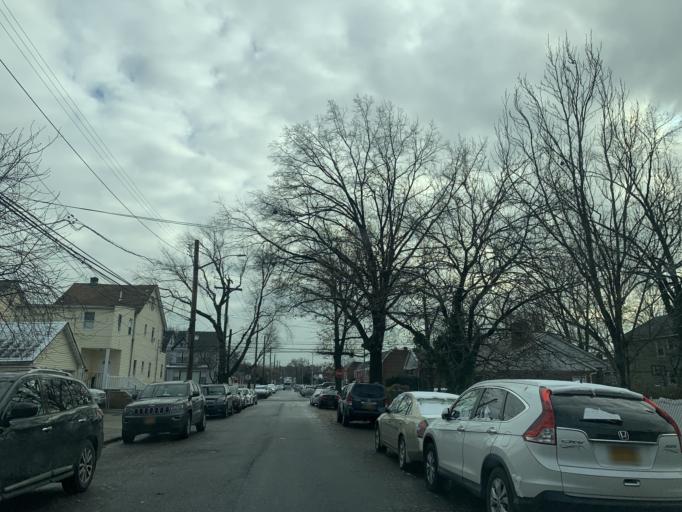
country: US
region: New York
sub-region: Queens County
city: Jamaica
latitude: 40.6879
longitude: -73.7800
